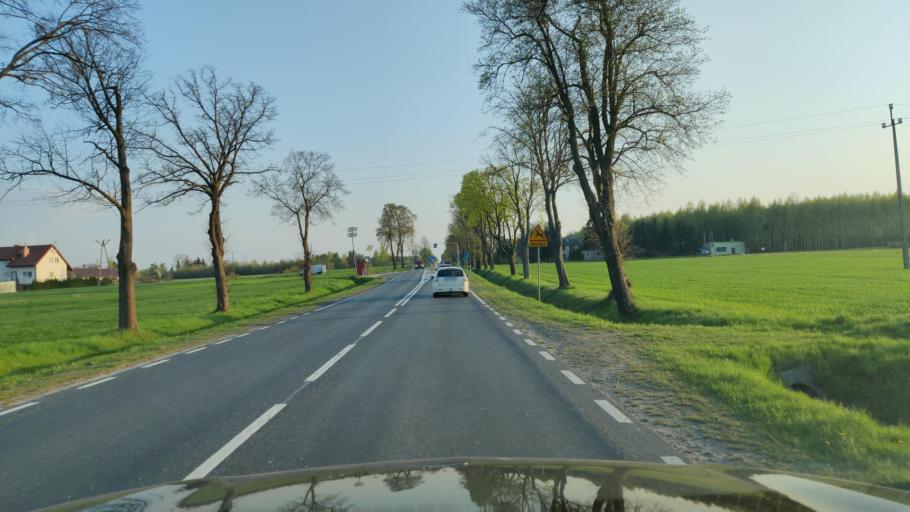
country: PL
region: Masovian Voivodeship
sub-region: Powiat pultuski
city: Zatory
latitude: 52.5865
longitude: 21.1016
